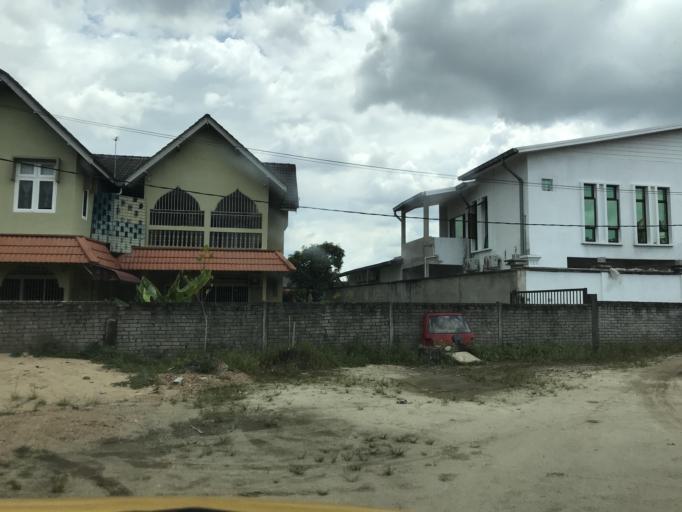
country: MY
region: Kelantan
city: Pasir Mas
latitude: 6.0497
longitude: 102.1798
